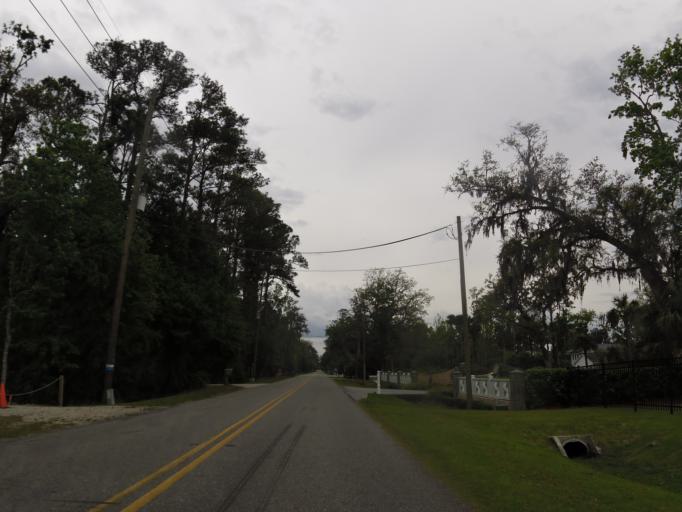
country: US
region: Florida
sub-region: Saint Johns County
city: Palm Valley
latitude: 30.1994
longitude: -81.4060
